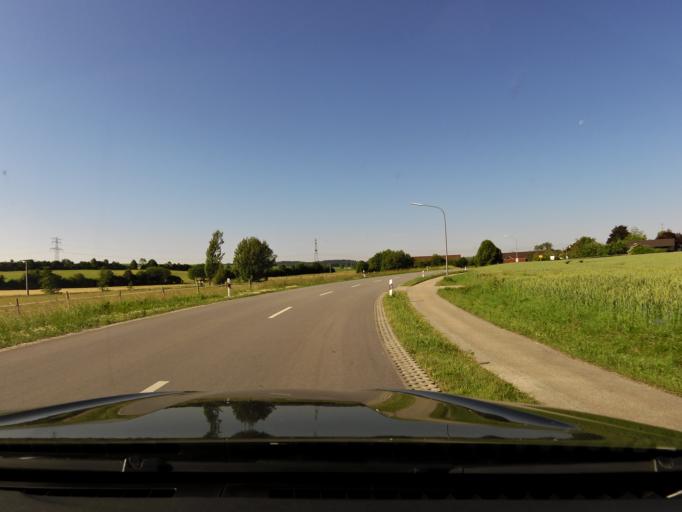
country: DE
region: Bavaria
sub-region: Upper Bavaria
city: Egglkofen
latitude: 48.4321
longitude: 12.4238
